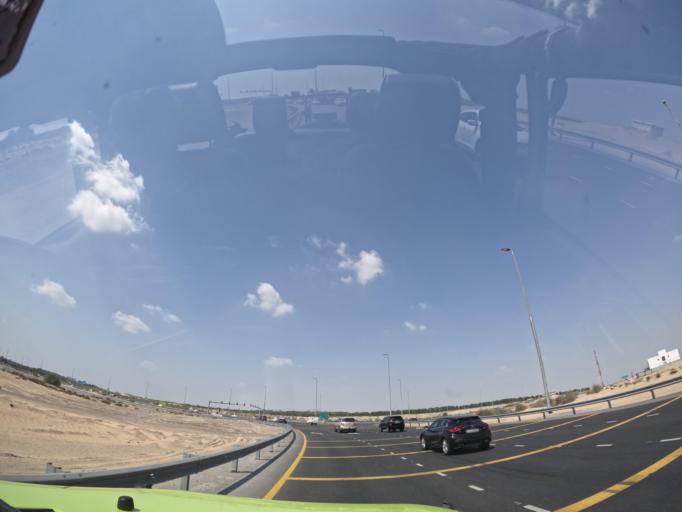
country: AE
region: Ash Shariqah
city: Sharjah
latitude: 25.1696
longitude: 55.4615
